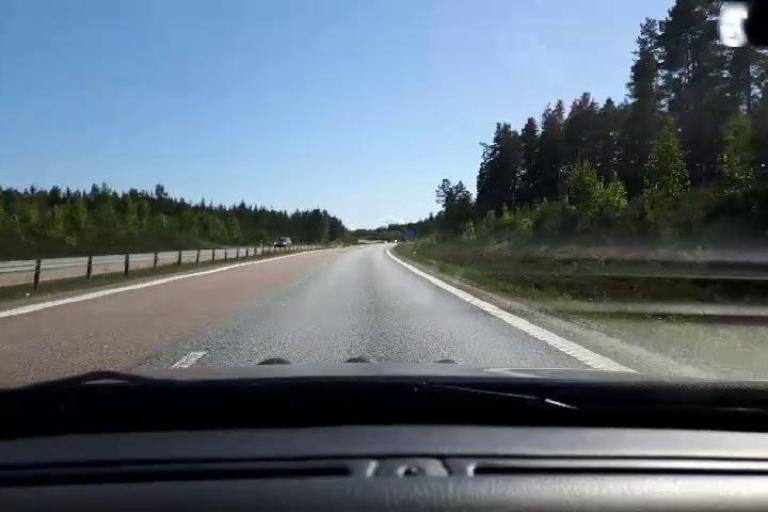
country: SE
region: Gaevleborg
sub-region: Soderhamns Kommun
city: Soderhamn
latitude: 61.3439
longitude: 17.0187
